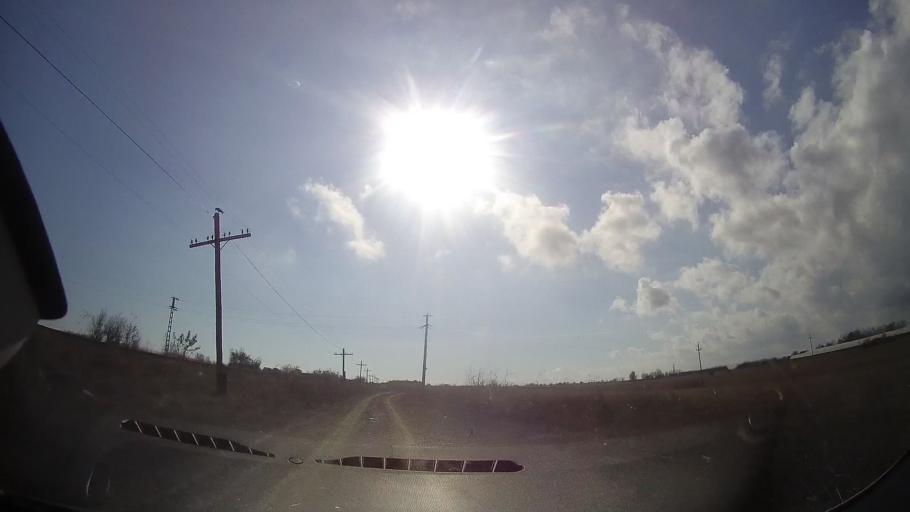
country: RO
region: Constanta
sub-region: Comuna Tuzla
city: Tuzla
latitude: 43.9942
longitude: 28.6454
